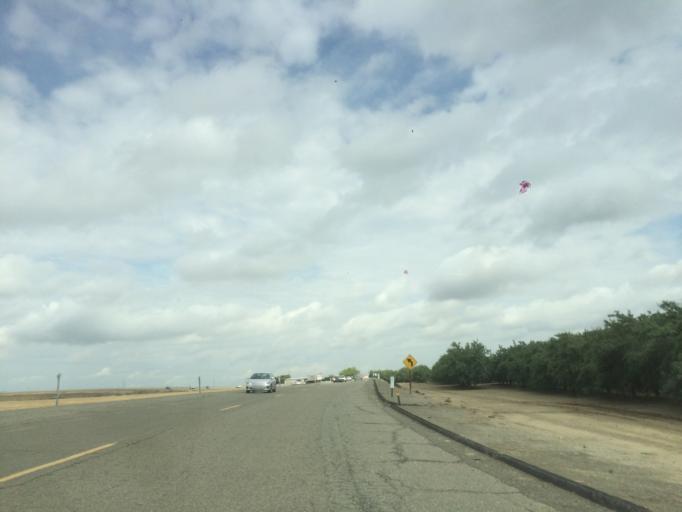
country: US
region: California
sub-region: Fresno County
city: Coalinga
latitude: 36.3659
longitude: -120.3308
